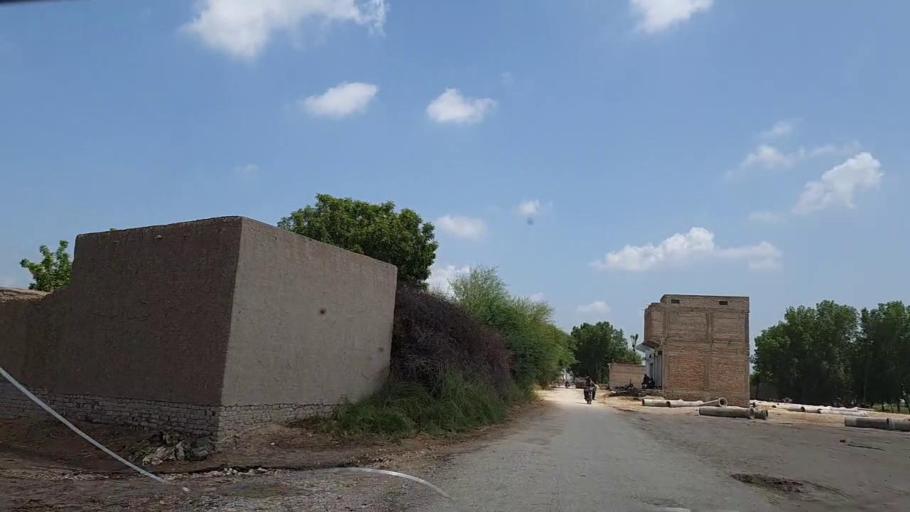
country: PK
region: Sindh
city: Tharu Shah
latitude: 26.9926
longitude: 68.0725
